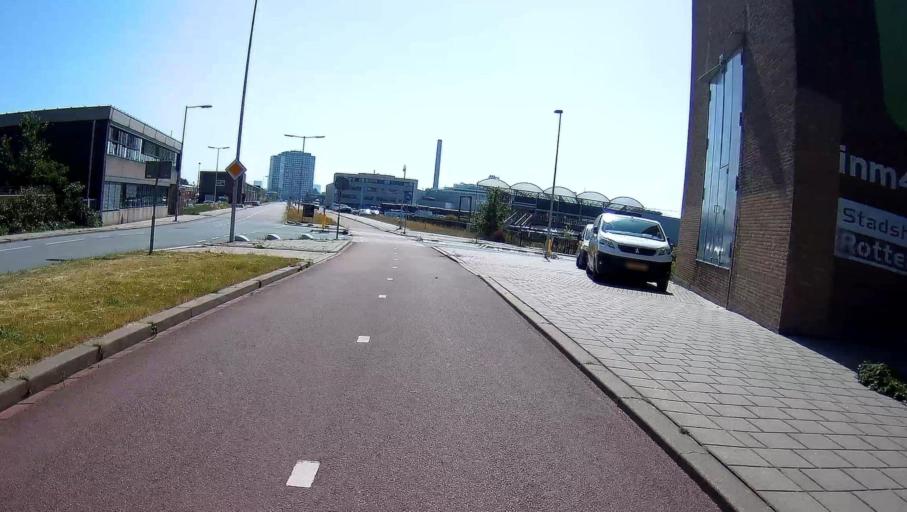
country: NL
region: South Holland
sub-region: Gemeente Schiedam
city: Schiedam
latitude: 51.9132
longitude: 4.4125
